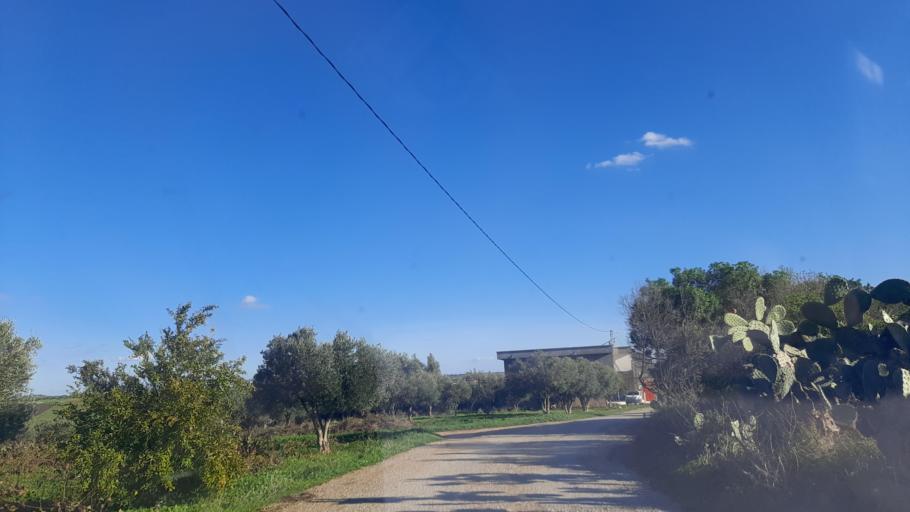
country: TN
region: Nabul
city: El Mida
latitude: 36.8377
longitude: 10.8316
